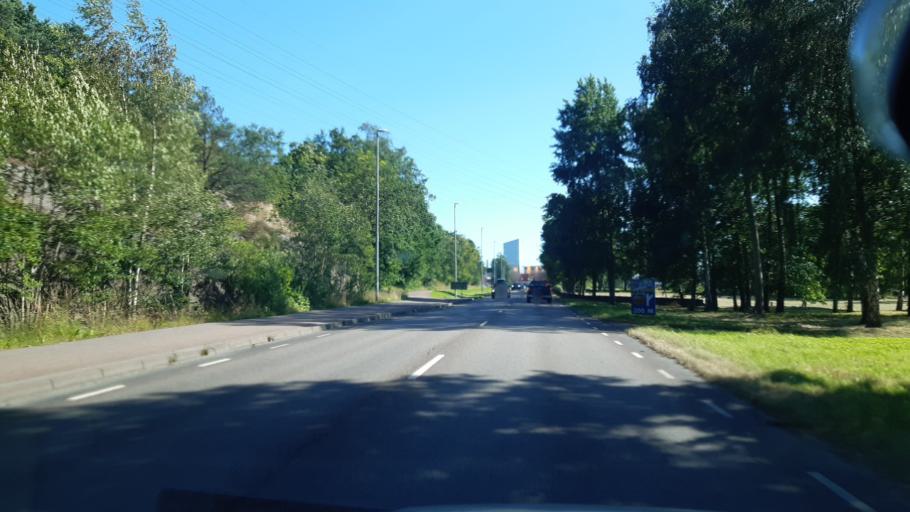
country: SE
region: Vaestra Goetaland
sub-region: Goteborg
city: Eriksbo
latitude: 57.7395
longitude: 12.0060
